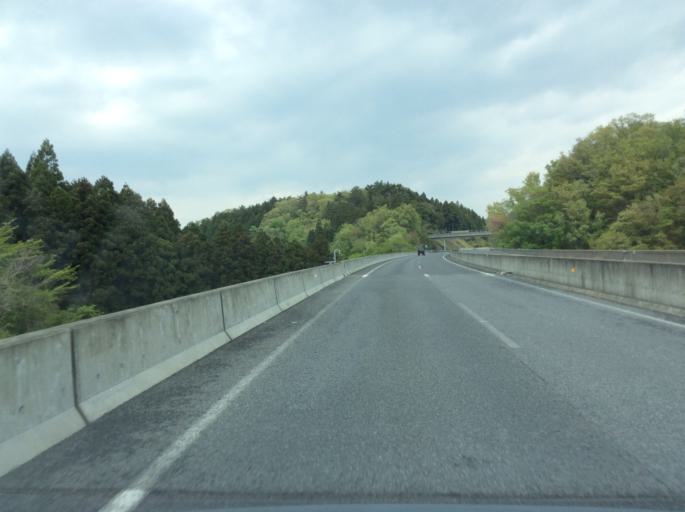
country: JP
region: Fukushima
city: Iwaki
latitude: 37.0692
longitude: 140.7919
